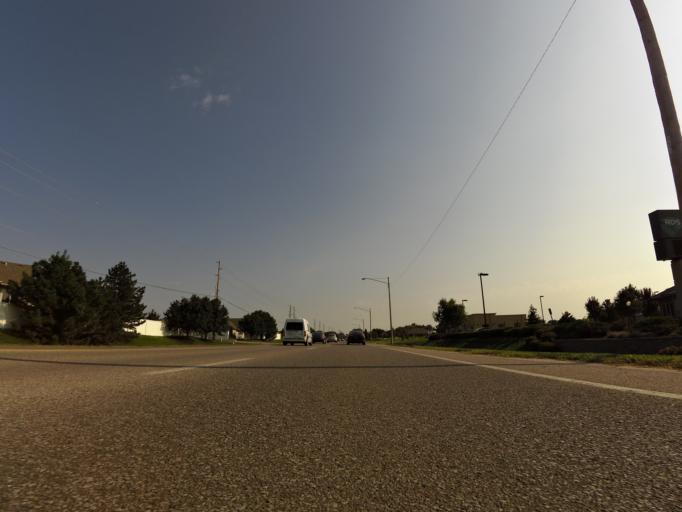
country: US
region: Kansas
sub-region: Sedgwick County
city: Maize
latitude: 37.7438
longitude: -97.4263
